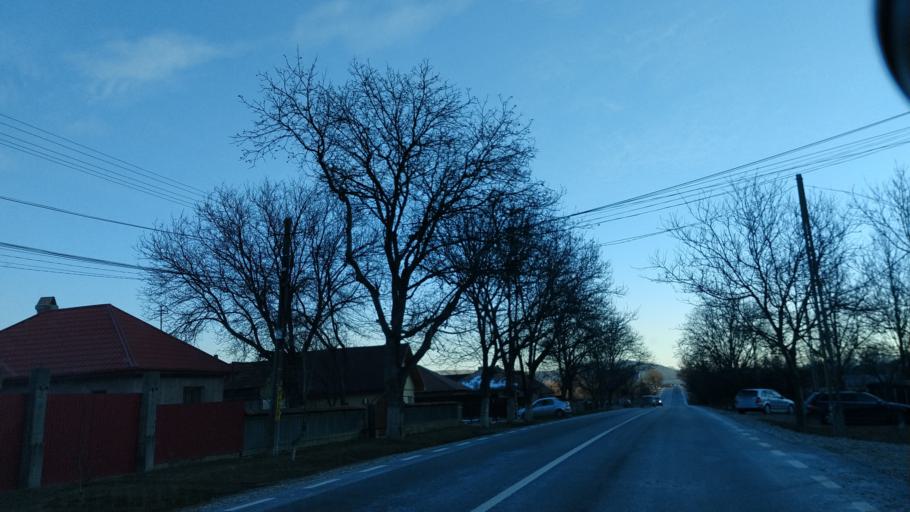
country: RO
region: Bacau
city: Gura Vaii
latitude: 46.3190
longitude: 26.7482
